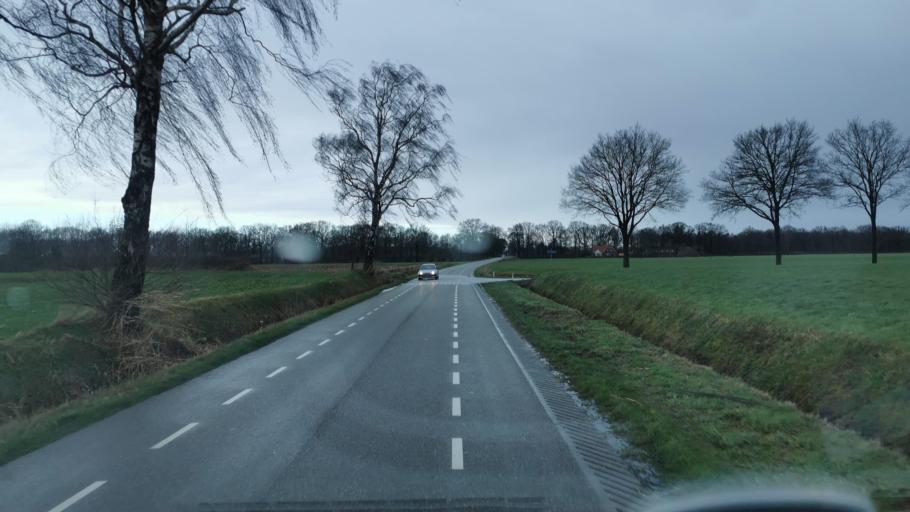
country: NL
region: Overijssel
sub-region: Gemeente Tubbergen
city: Tubbergen
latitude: 52.3681
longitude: 6.8523
